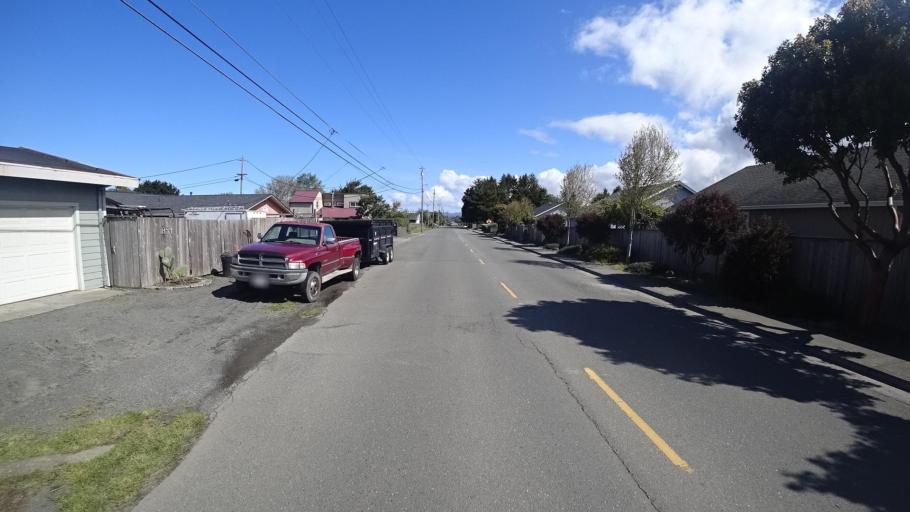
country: US
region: California
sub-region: Humboldt County
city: McKinleyville
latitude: 40.9399
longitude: -124.1107
